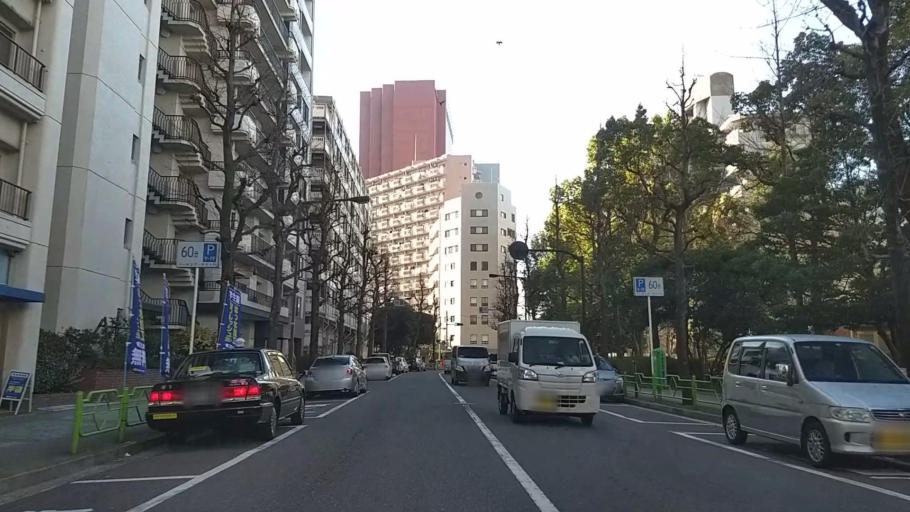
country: JP
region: Tokyo
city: Tokyo
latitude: 35.6660
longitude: 139.7773
